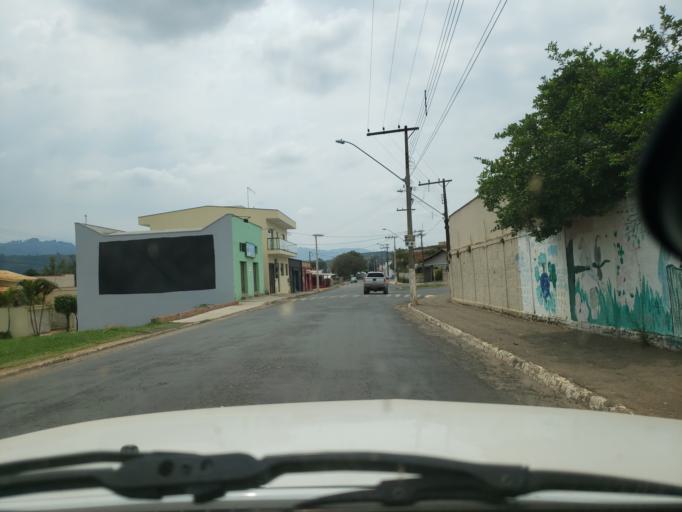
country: BR
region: Minas Gerais
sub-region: Jacutinga
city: Jacutinga
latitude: -22.2796
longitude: -46.6072
